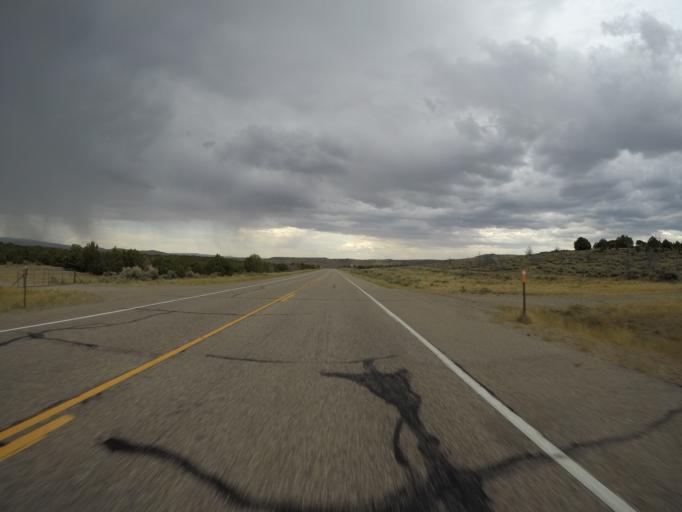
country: US
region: Colorado
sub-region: Rio Blanco County
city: Rangely
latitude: 40.3824
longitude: -108.3558
